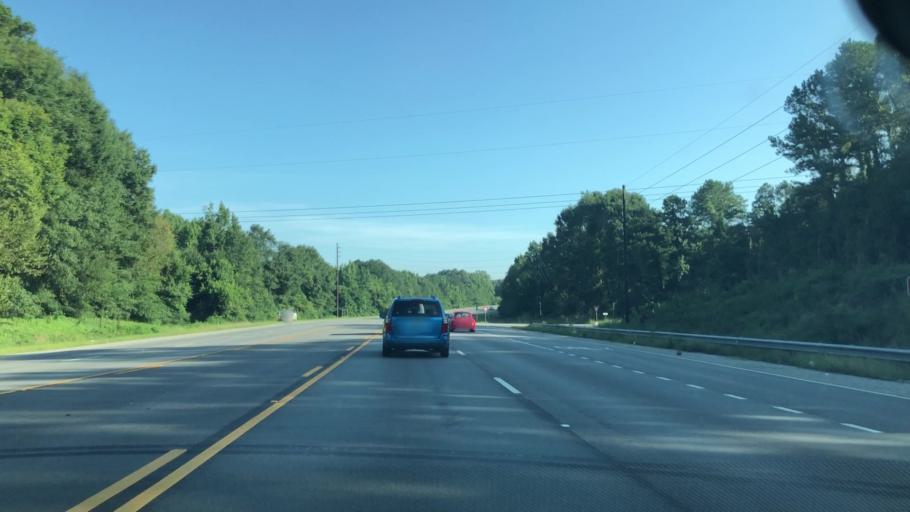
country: US
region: Alabama
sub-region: Calhoun County
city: Bynum
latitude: 33.6062
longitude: -85.9280
